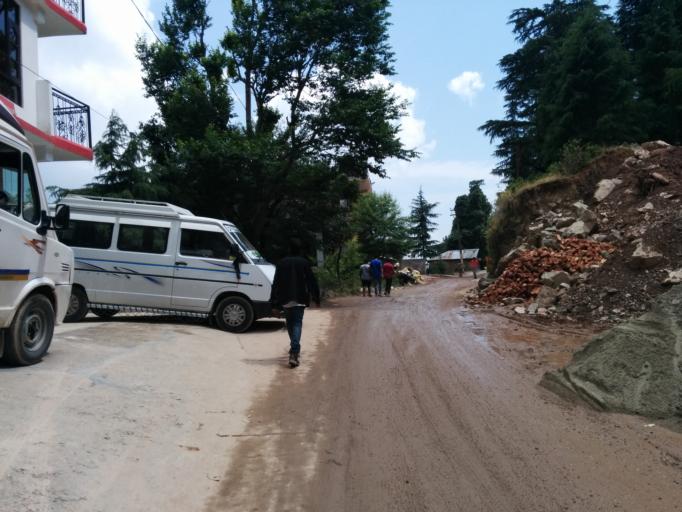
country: IN
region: Himachal Pradesh
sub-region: Kangra
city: Dharmsala
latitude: 32.2426
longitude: 76.3321
